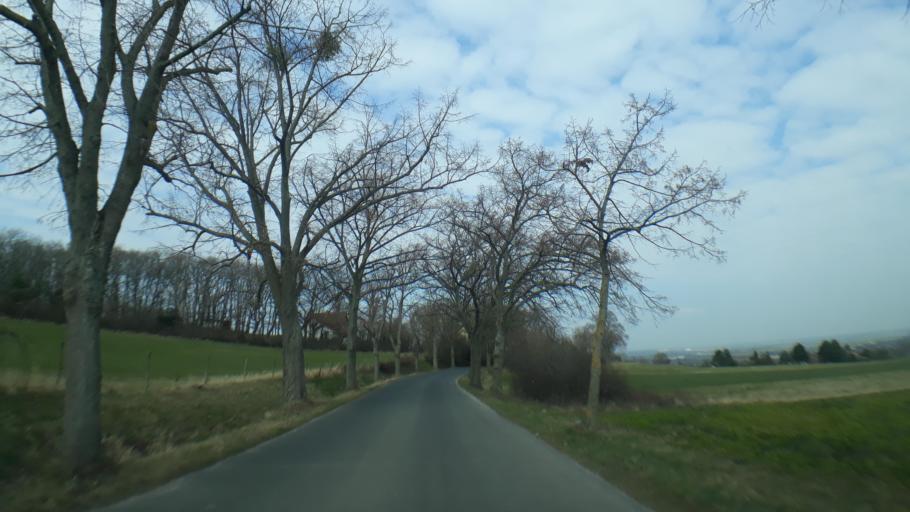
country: DE
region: North Rhine-Westphalia
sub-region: Regierungsbezirk Koln
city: Euskirchen
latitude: 50.6029
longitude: 6.8257
